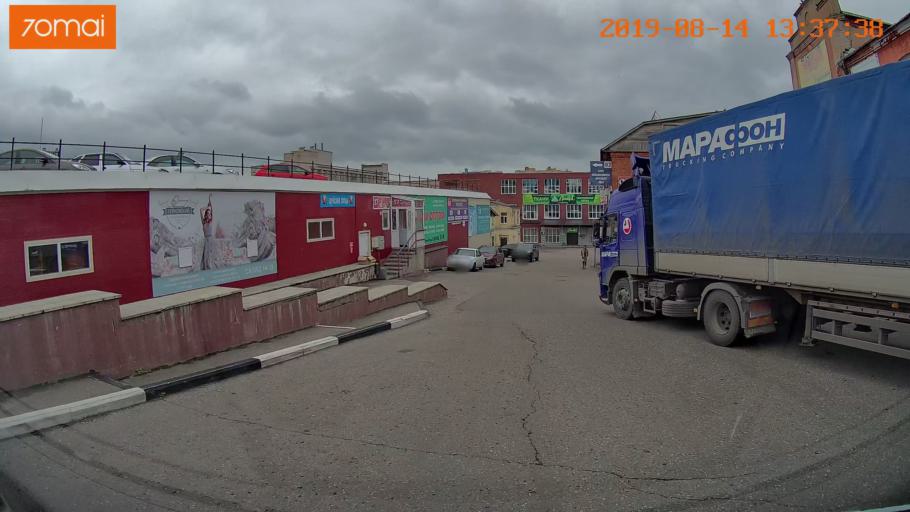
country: RU
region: Ivanovo
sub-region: Gorod Ivanovo
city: Ivanovo
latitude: 57.0093
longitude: 40.9678
